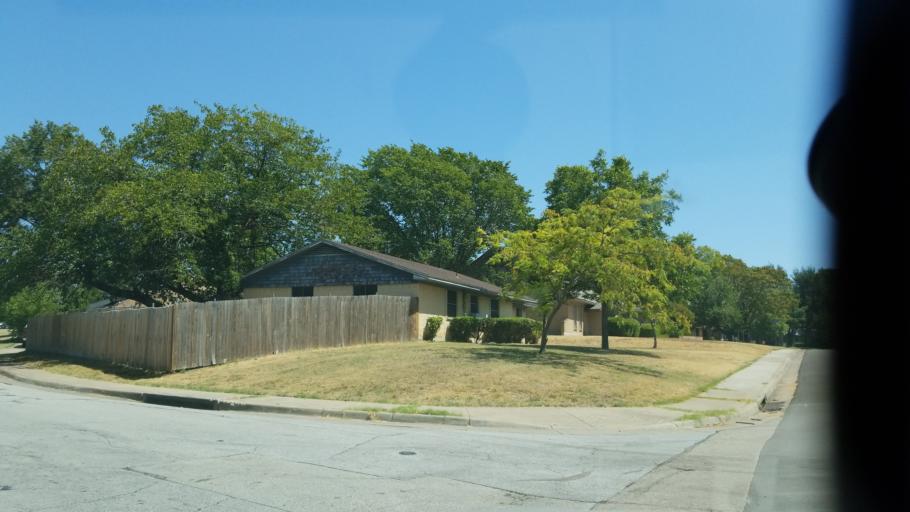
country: US
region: Texas
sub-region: Dallas County
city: Duncanville
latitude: 32.6527
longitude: -96.8995
